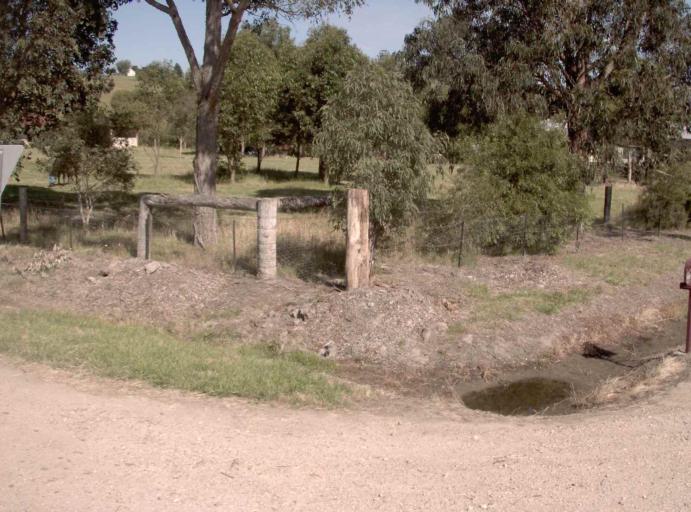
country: AU
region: Victoria
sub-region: East Gippsland
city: Bairnsdale
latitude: -37.7274
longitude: 147.8085
